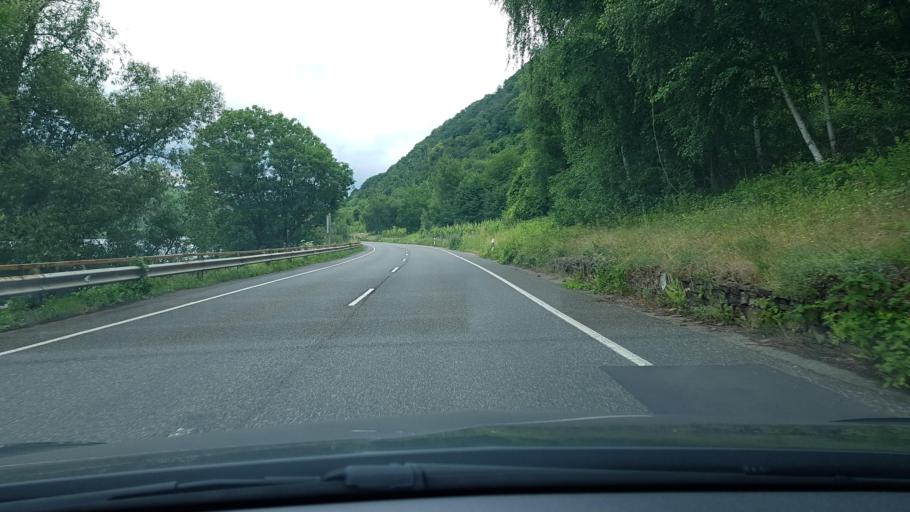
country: DE
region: Rheinland-Pfalz
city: Winningen
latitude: 50.3109
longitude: 7.5219
